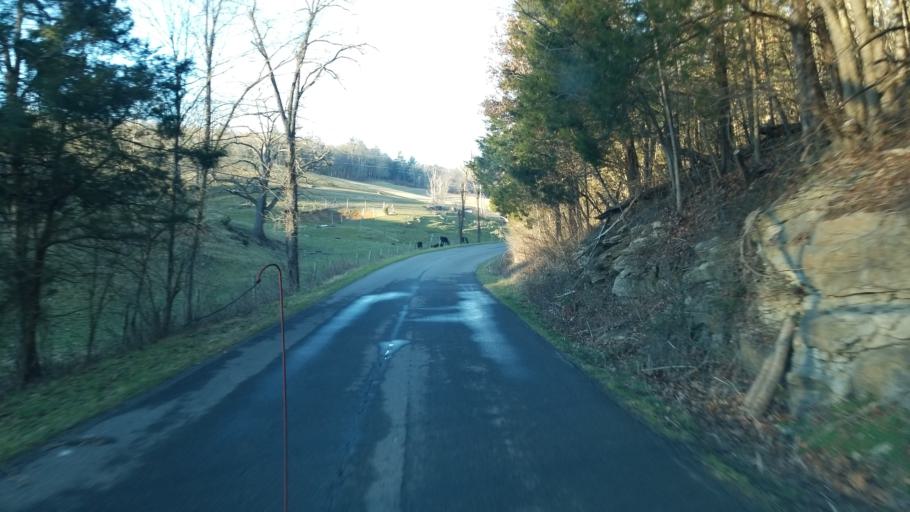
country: US
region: Virginia
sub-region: Pulaski County
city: Pulaski
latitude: 37.1837
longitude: -80.8388
